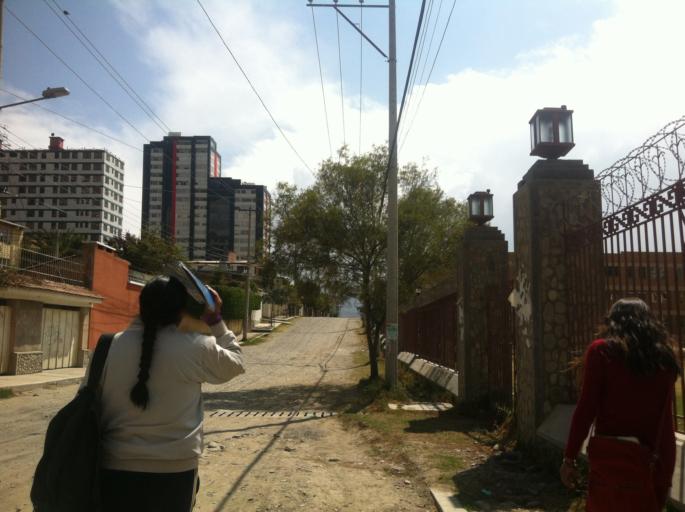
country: BO
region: La Paz
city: La Paz
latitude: -16.5396
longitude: -68.0667
